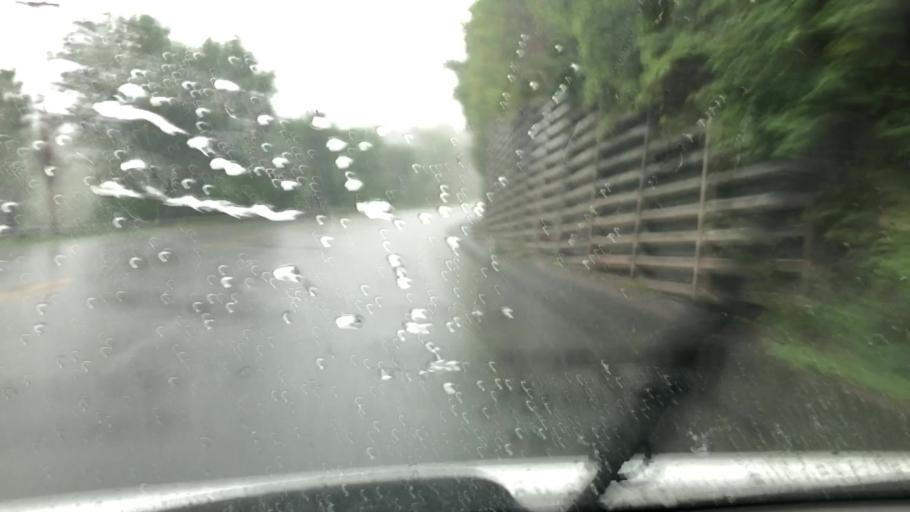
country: US
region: Massachusetts
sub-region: Berkshire County
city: Adams
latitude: 42.5957
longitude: -73.1412
